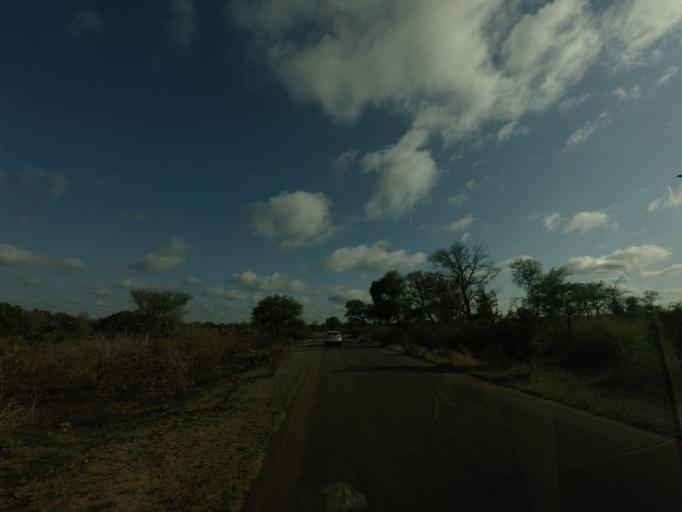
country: ZA
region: Mpumalanga
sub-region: Ehlanzeni District
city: Komatipoort
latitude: -25.2437
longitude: 31.8501
